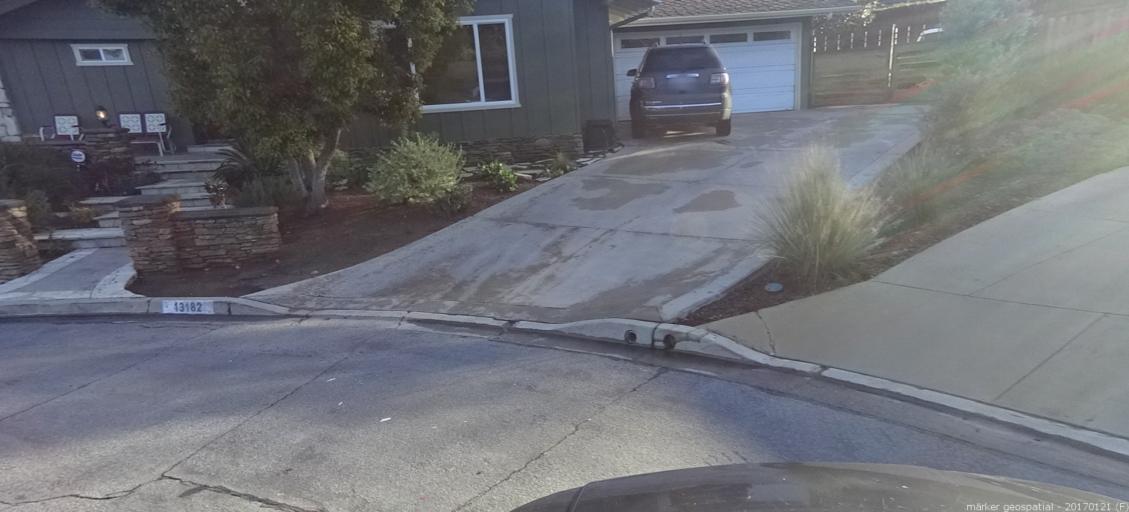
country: US
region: California
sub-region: Orange County
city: North Tustin
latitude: 33.7706
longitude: -117.8098
